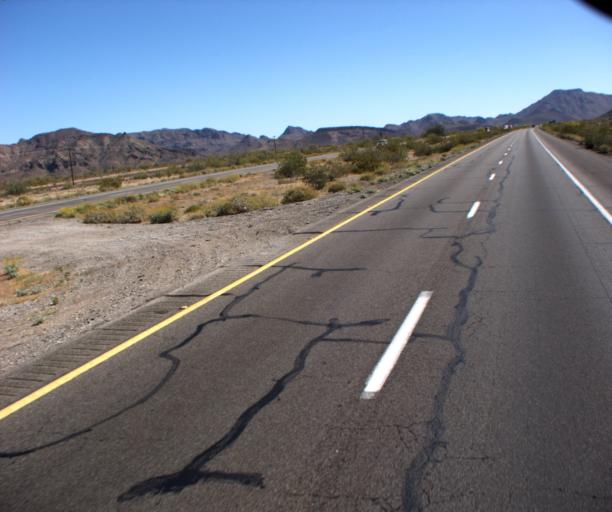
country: US
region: Arizona
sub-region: La Paz County
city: Quartzsite
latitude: 33.6778
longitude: -114.1119
